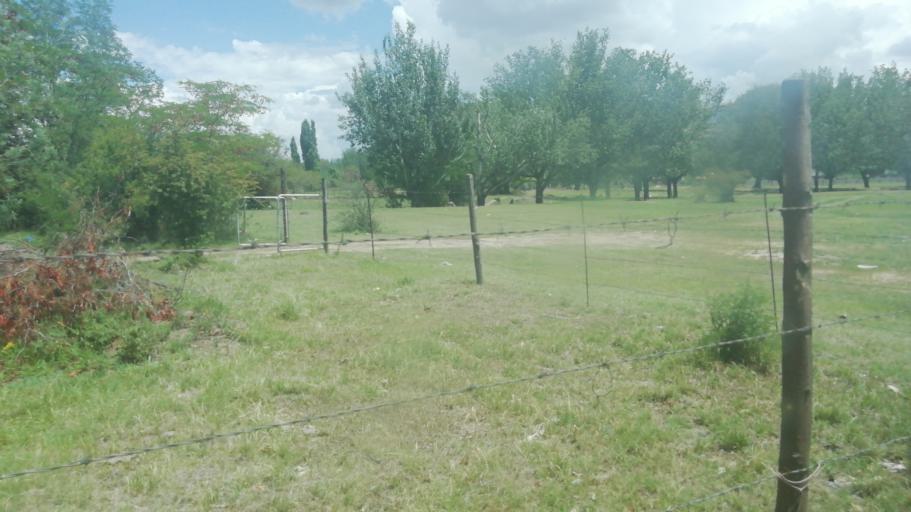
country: LS
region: Maseru
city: Nako
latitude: -29.6207
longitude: 27.5091
